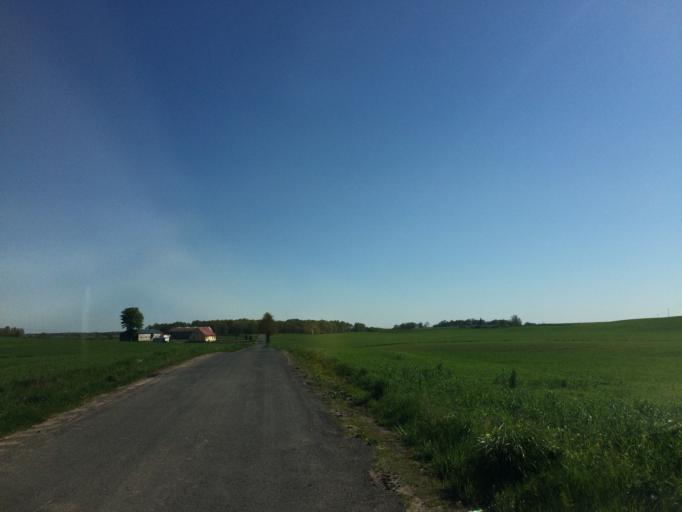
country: PL
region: Warmian-Masurian Voivodeship
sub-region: Powiat dzialdowski
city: Rybno
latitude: 53.4510
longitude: 19.9283
